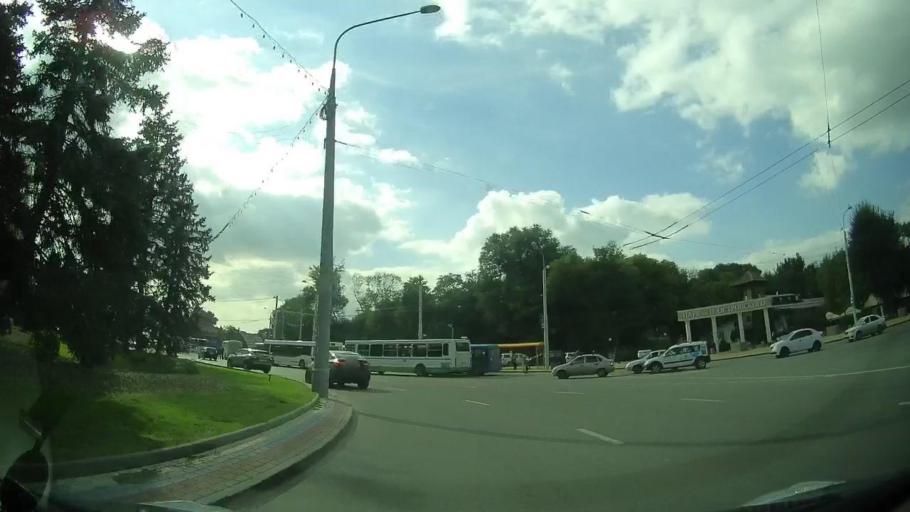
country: RU
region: Rostov
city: Imeni Chkalova
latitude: 47.2573
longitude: 39.8014
